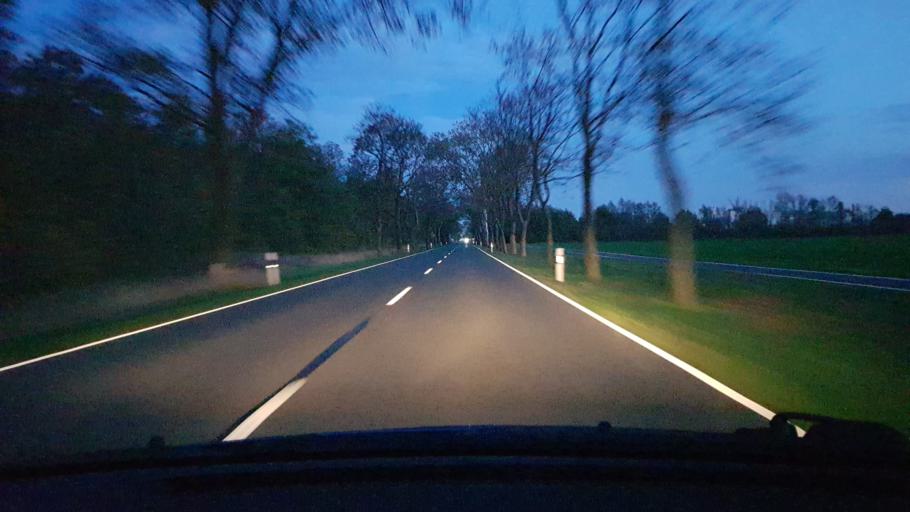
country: DE
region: Saxony-Anhalt
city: Rodleben
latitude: 51.9059
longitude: 12.2052
